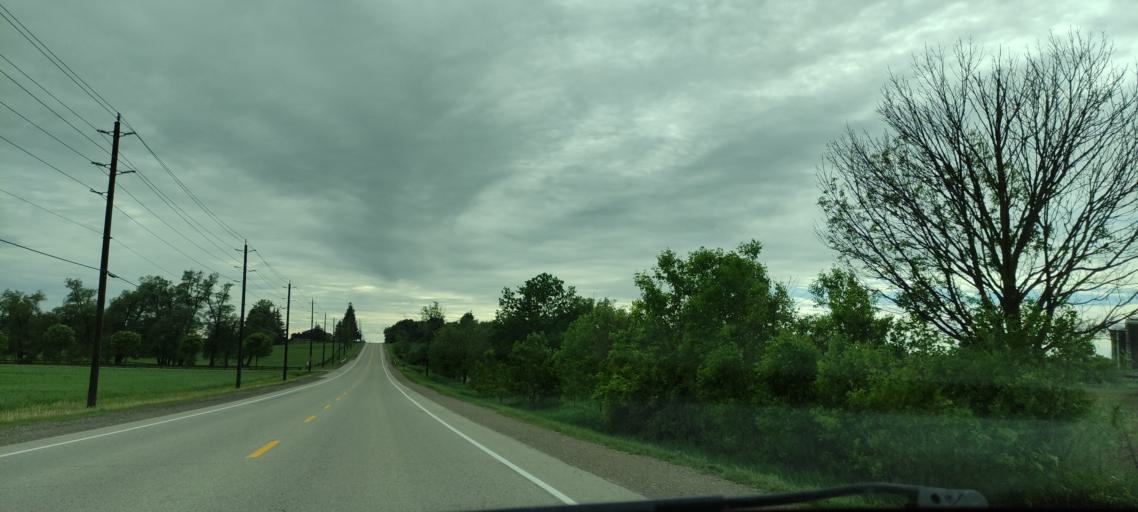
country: CA
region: Ontario
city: Kitchener
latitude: 43.3820
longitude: -80.6523
